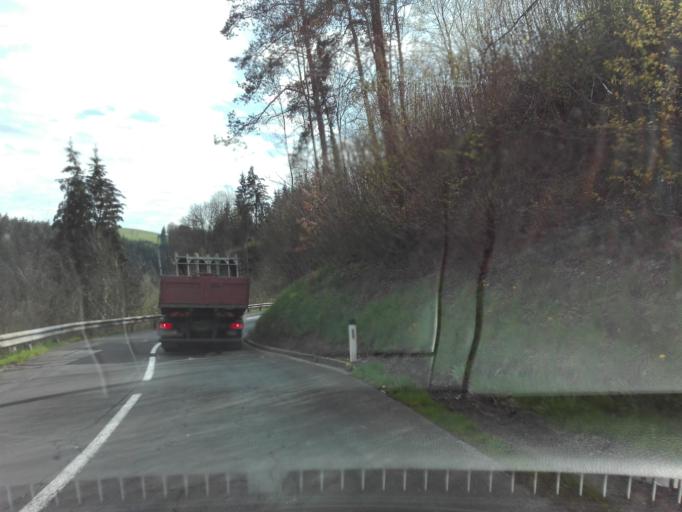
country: AT
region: Upper Austria
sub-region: Politischer Bezirk Rohrbach
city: Kleinzell im Muehlkreis
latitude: 48.4847
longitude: 14.0039
